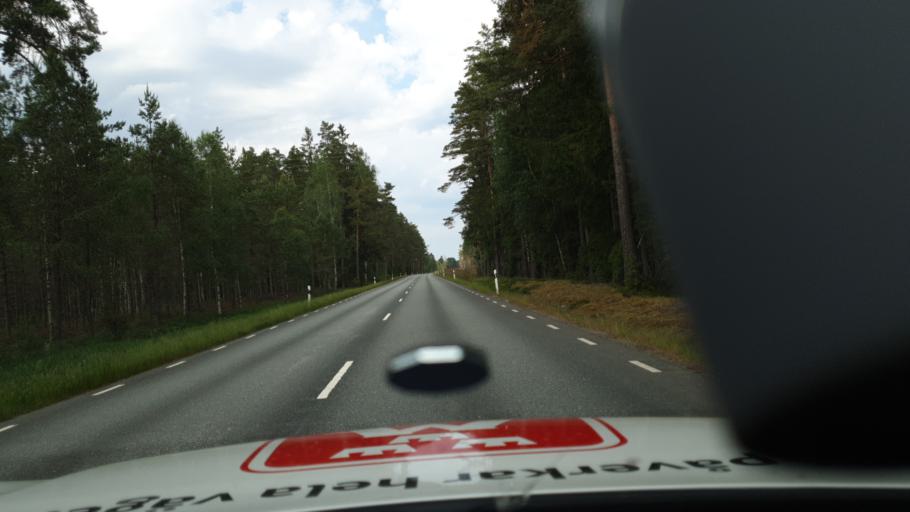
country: SE
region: Joenkoeping
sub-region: Varnamo Kommun
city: Varnamo
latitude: 57.2870
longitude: 14.0695
